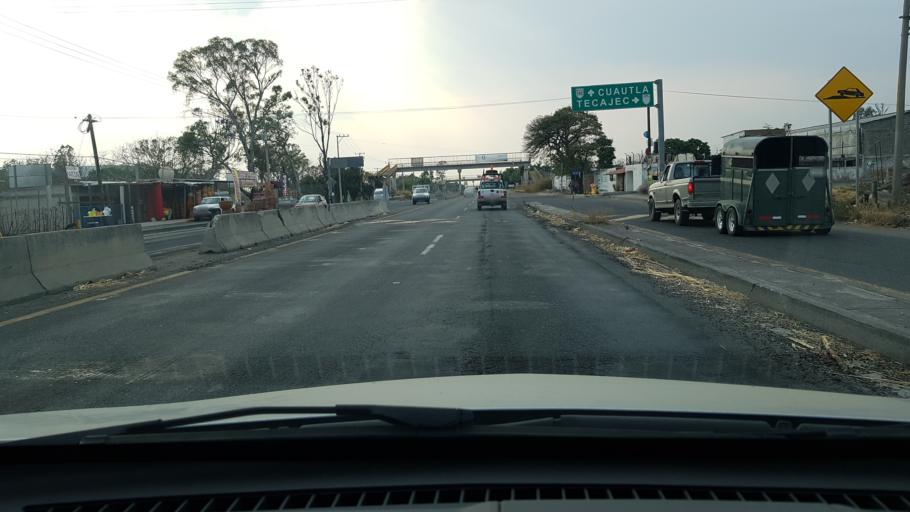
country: MX
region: Morelos
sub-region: Ayala
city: Unidad Habitacional Mariano Matamoros
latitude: 18.7447
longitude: -98.8393
